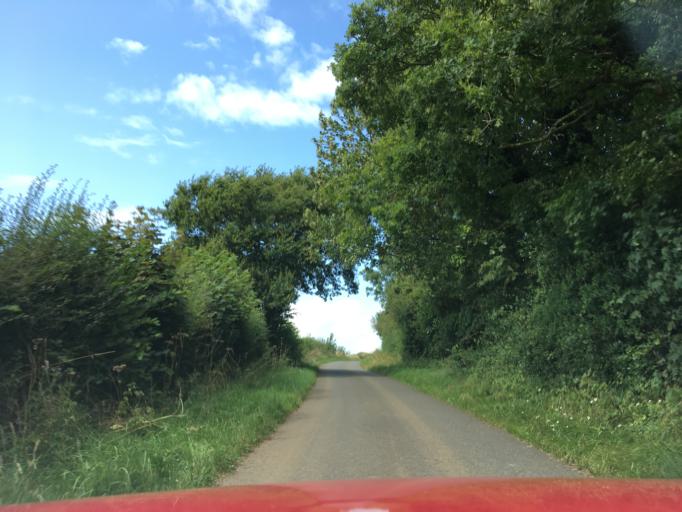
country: GB
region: England
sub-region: Wiltshire
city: Luckington
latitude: 51.6095
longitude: -2.2516
